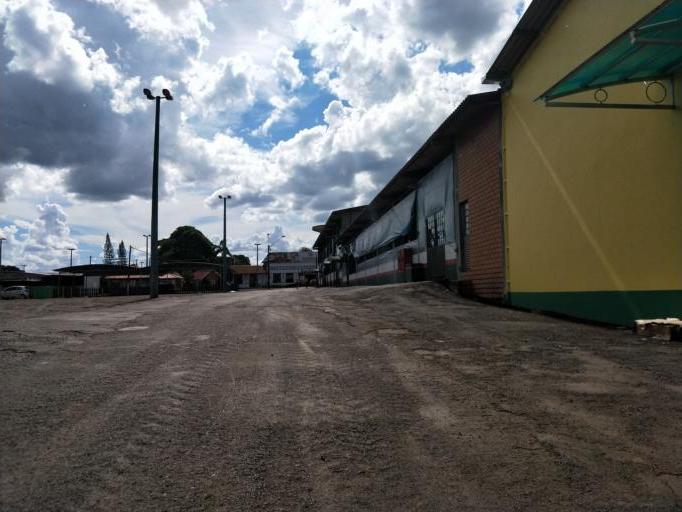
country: BR
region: Parana
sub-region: Marechal Candido Rondon
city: Marechal Candido Rondon
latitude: -24.5526
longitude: -54.0491
